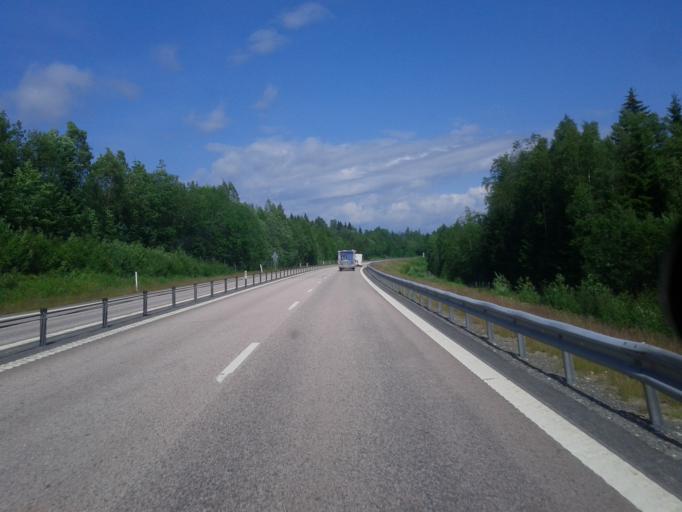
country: SE
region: Vaesternorrland
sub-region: OErnskoeldsviks Kommun
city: Husum
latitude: 63.4210
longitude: 19.2049
